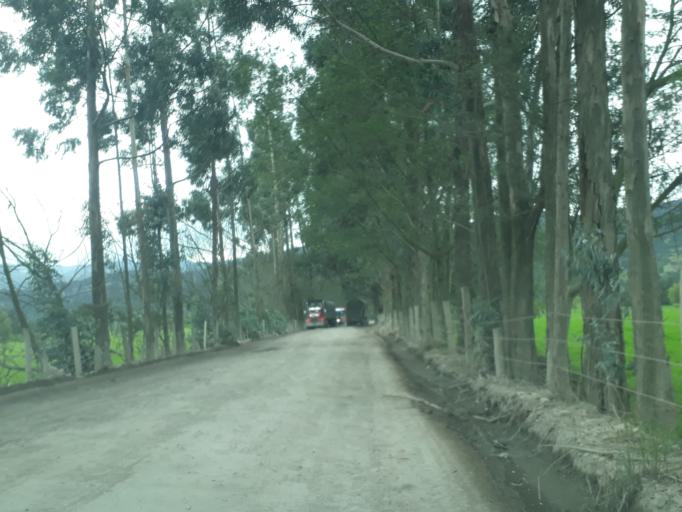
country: CO
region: Cundinamarca
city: Lenguazaque
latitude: 5.3349
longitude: -73.7105
